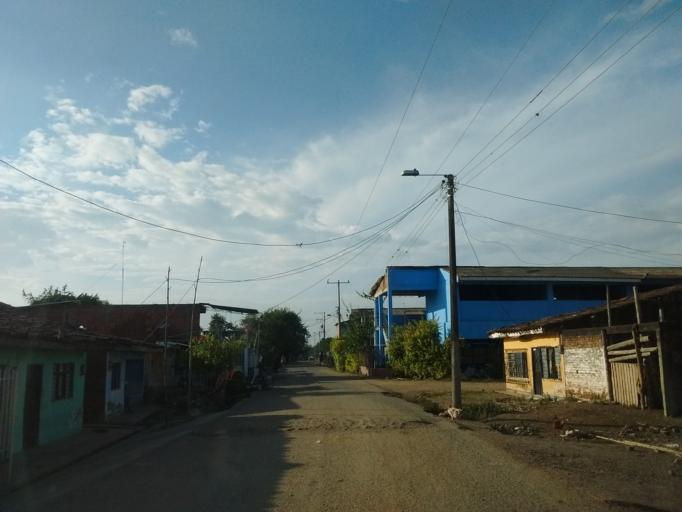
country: CO
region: Cauca
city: Puerto Tejada
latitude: 3.2204
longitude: -76.4433
